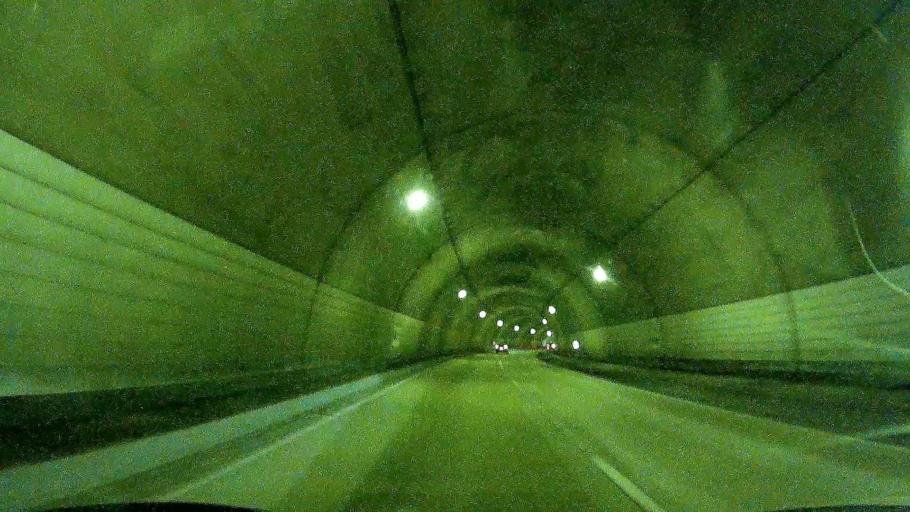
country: JP
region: Niigata
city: Tokamachi
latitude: 37.0068
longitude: 138.6420
